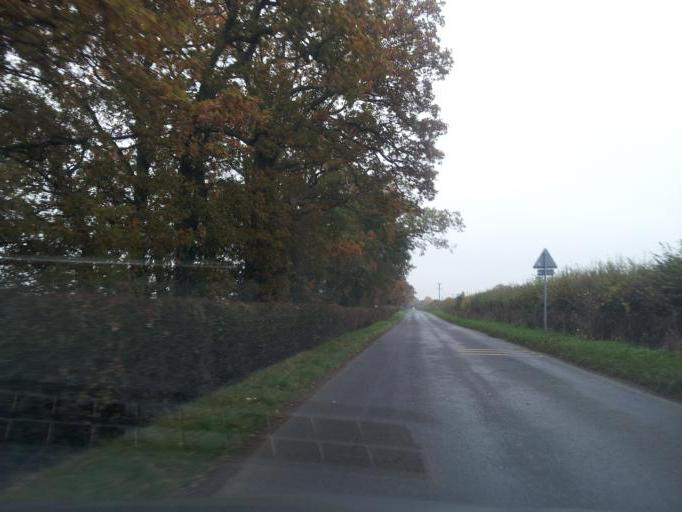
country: GB
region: England
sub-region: Milton Keynes
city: Shenley Church End
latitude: 51.9962
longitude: -0.8198
